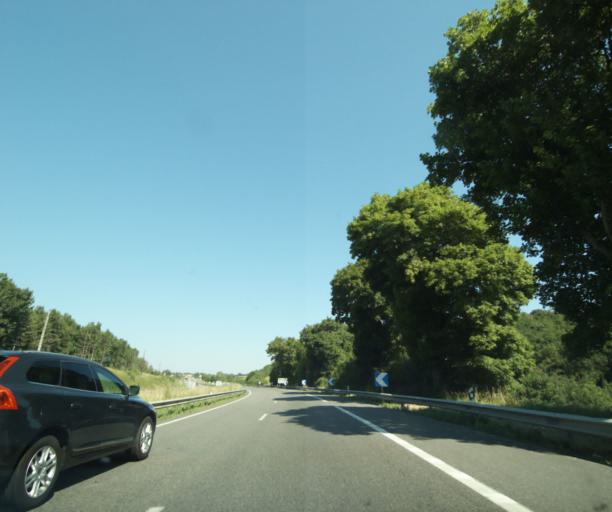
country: FR
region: Lorraine
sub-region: Departement de la Meuse
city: Vacon
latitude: 48.6941
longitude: 5.5489
